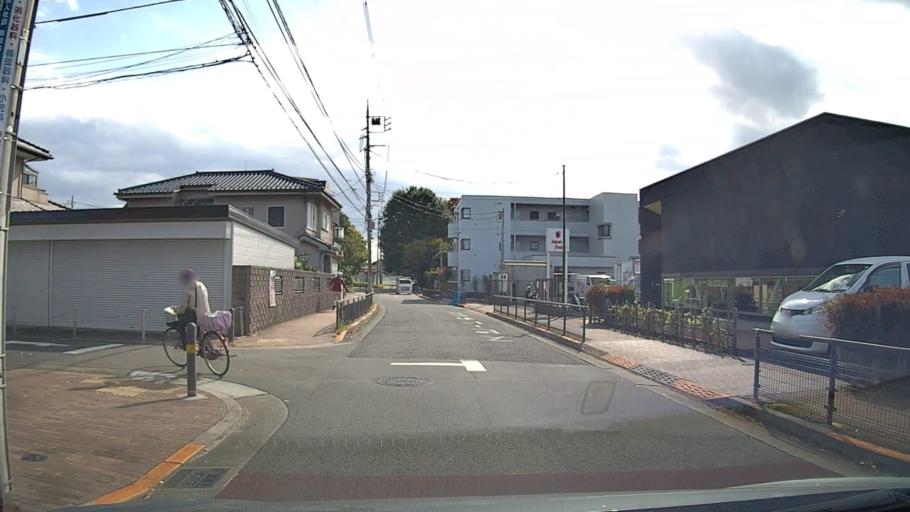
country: JP
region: Saitama
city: Wako
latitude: 35.7488
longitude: 139.6330
